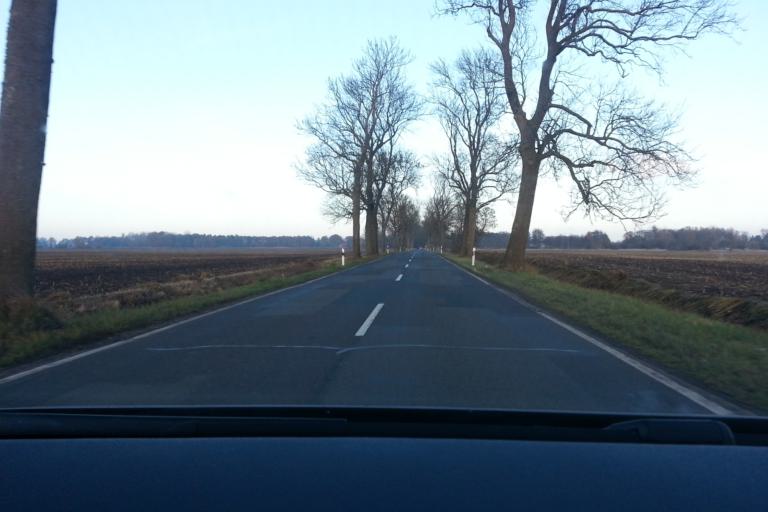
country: DE
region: Mecklenburg-Vorpommern
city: Ferdinandshof
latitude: 53.6492
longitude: 13.8672
